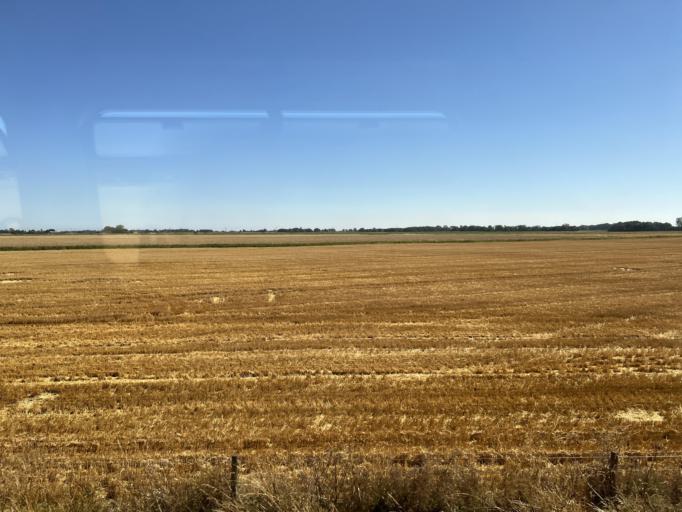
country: GB
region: England
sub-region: Lincolnshire
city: Spilsby
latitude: 53.1196
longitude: 0.1355
